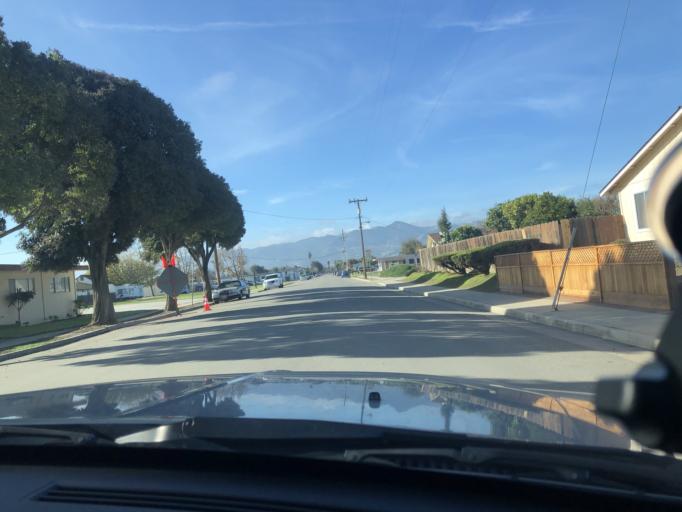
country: US
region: California
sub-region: Monterey County
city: King City
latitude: 36.2171
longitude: -121.1319
